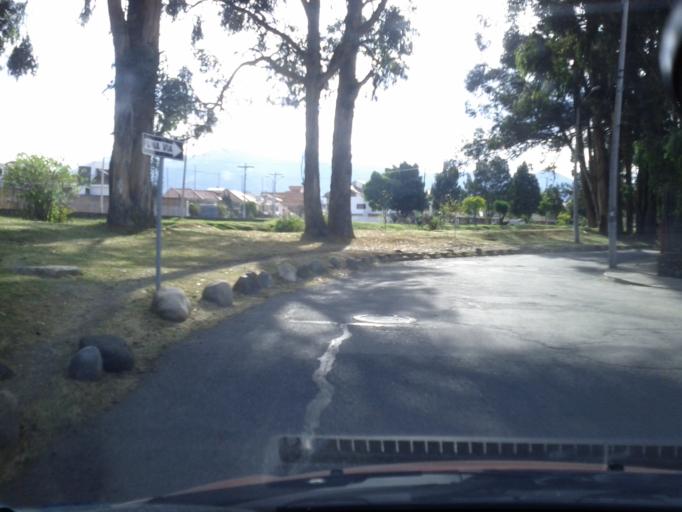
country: EC
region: Azuay
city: Cuenca
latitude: -2.8936
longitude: -79.0261
